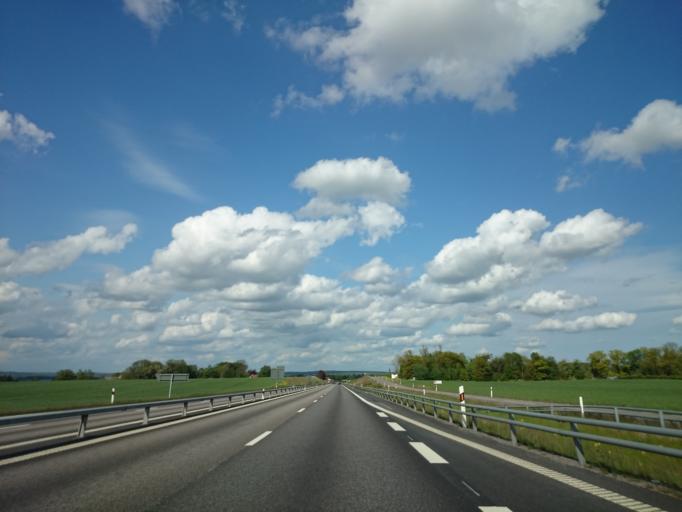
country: SE
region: Skane
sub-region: Hoors Kommun
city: Loberod
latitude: 55.8285
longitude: 13.5438
